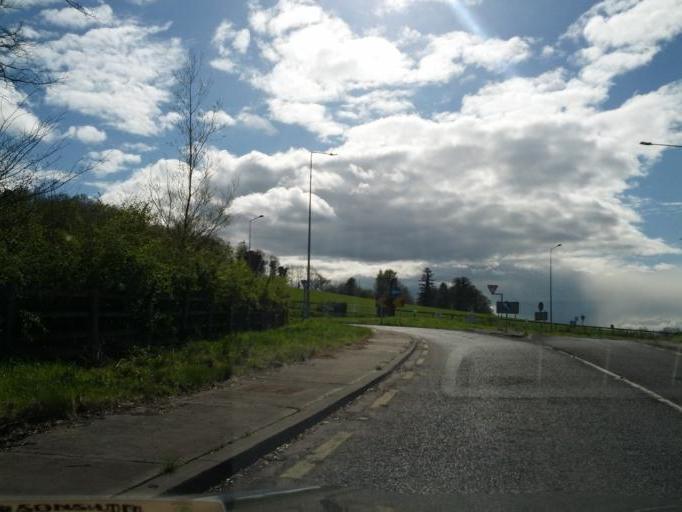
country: IE
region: Leinster
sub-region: An Mhi
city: Newtown Trim
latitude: 53.4796
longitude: -6.7199
